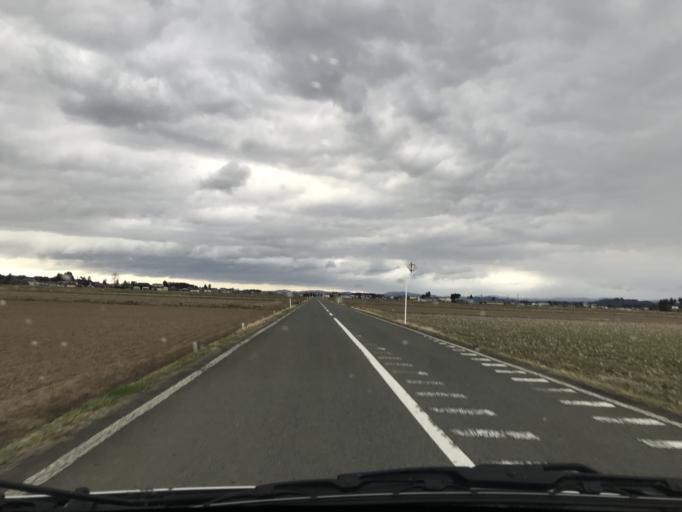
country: JP
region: Iwate
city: Mizusawa
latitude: 39.0933
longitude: 141.1629
